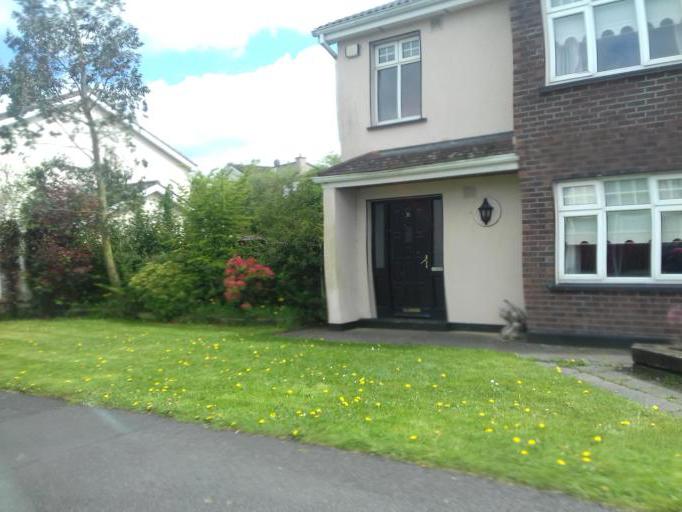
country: IE
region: Leinster
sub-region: Laois
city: Portlaoise
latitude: 53.0453
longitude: -7.3127
